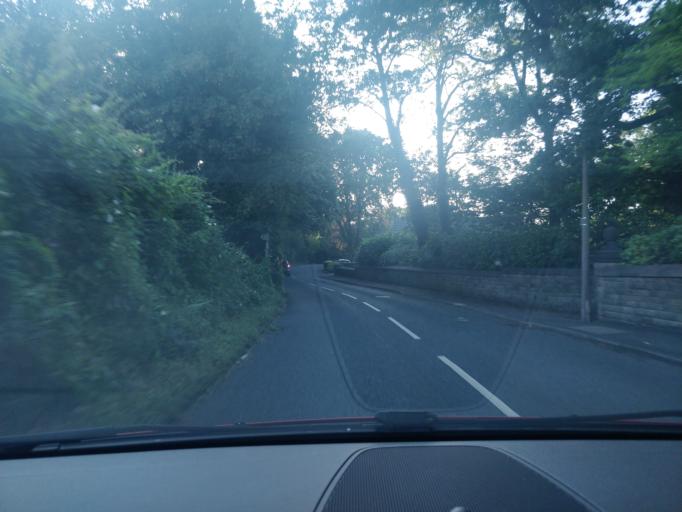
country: GB
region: England
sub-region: Lancashire
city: Parbold
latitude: 53.5835
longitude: -2.7733
